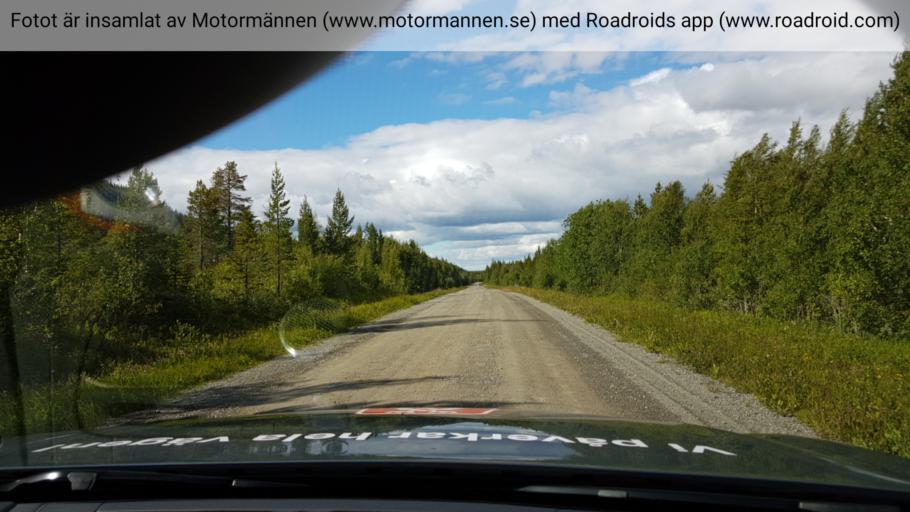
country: SE
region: Jaemtland
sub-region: Krokoms Kommun
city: Valla
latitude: 63.0593
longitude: 13.9622
